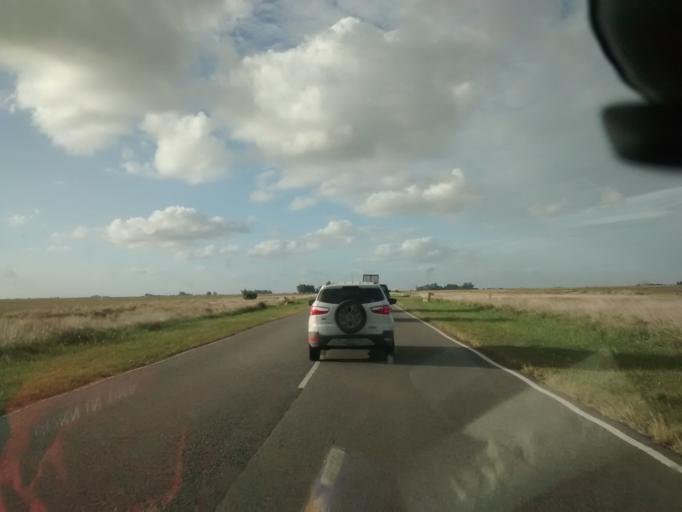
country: AR
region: Buenos Aires
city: Pila
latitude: -36.3442
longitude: -58.5811
